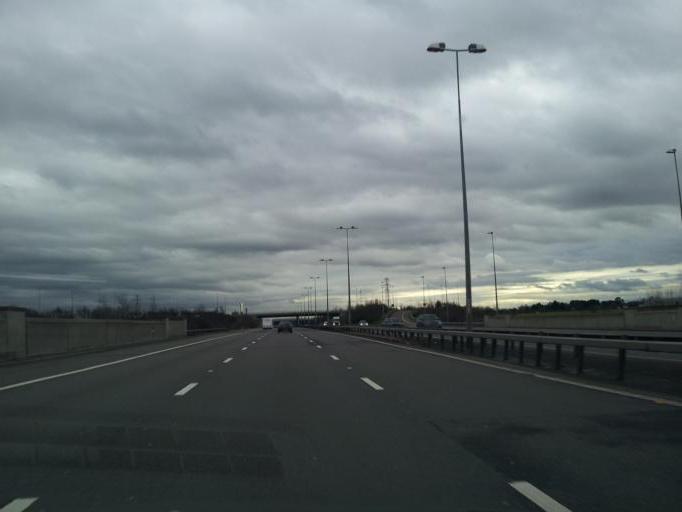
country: GB
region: England
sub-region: Warwickshire
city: Curdworth
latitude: 52.5415
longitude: -1.7294
